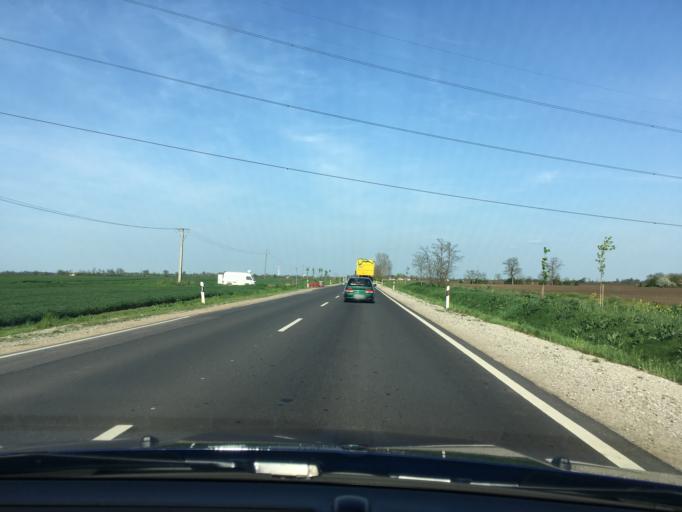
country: HU
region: Bekes
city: Ujkigyos
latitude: 46.6687
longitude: 20.9817
